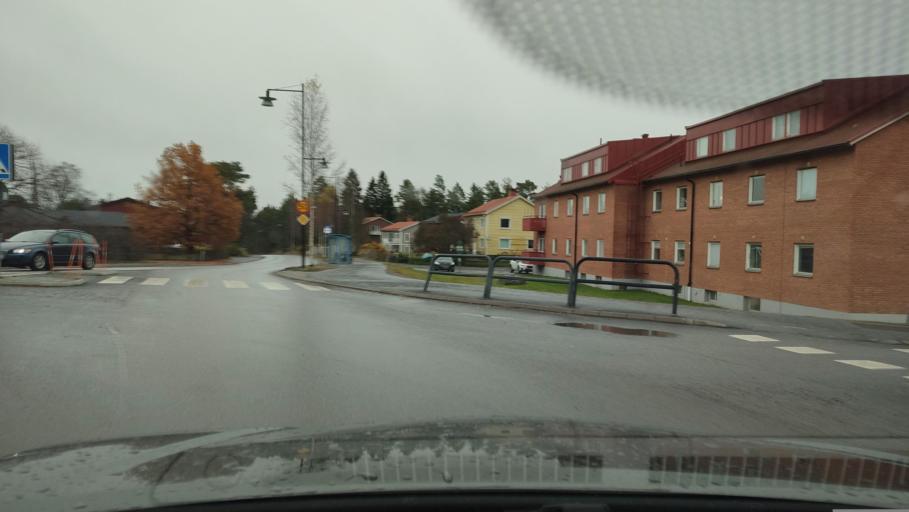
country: SE
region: Vaesterbotten
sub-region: Umea Kommun
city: Holmsund
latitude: 63.7128
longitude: 20.3788
